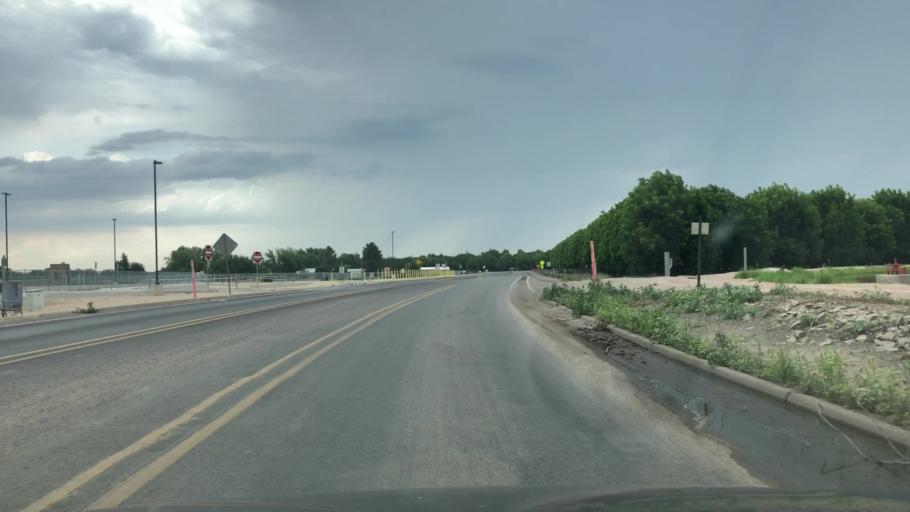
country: US
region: New Mexico
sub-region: Dona Ana County
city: La Union
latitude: 31.9988
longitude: -106.6560
